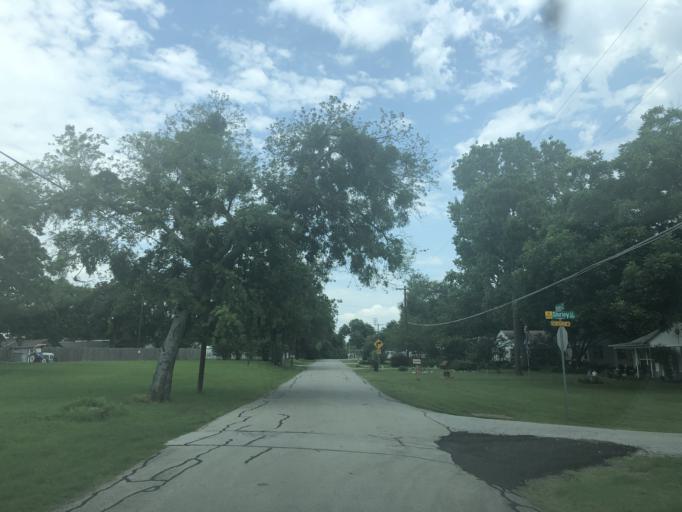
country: US
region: Texas
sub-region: Dallas County
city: Irving
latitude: 32.7912
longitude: -96.9419
